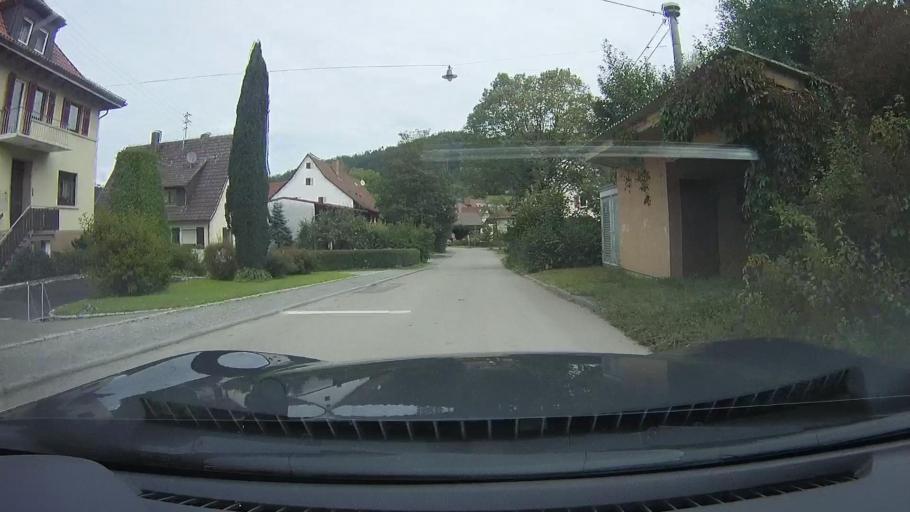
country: DE
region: Baden-Wuerttemberg
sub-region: Regierungsbezirk Stuttgart
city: Murrhardt
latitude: 48.9929
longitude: 9.5372
